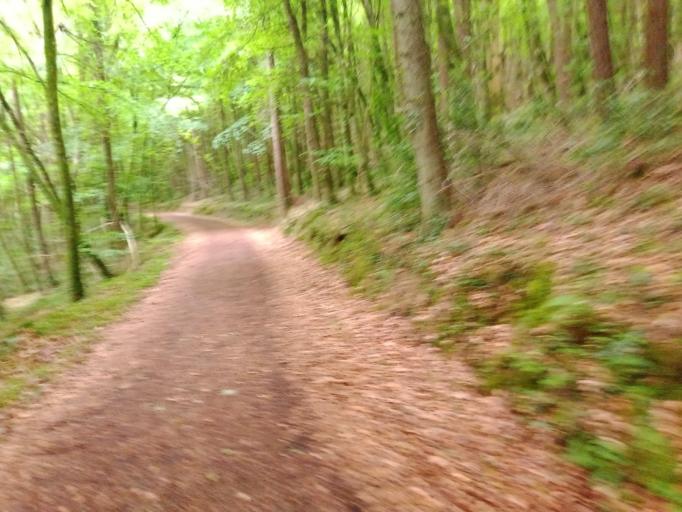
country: IE
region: Leinster
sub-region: Laois
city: Stradbally
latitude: 52.9996
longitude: -7.1174
